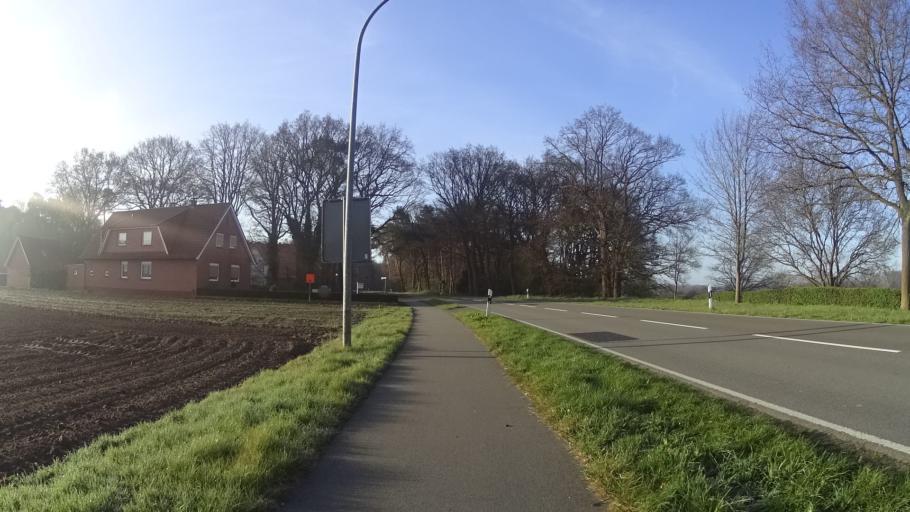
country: DE
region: Lower Saxony
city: Lathen
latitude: 52.8780
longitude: 7.3158
